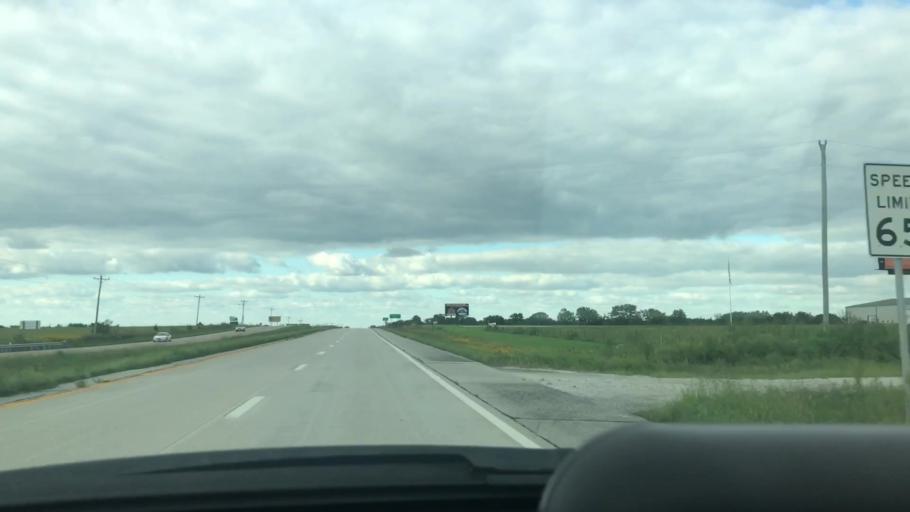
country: US
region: Missouri
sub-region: Benton County
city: Lincoln
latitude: 38.3427
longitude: -93.3404
